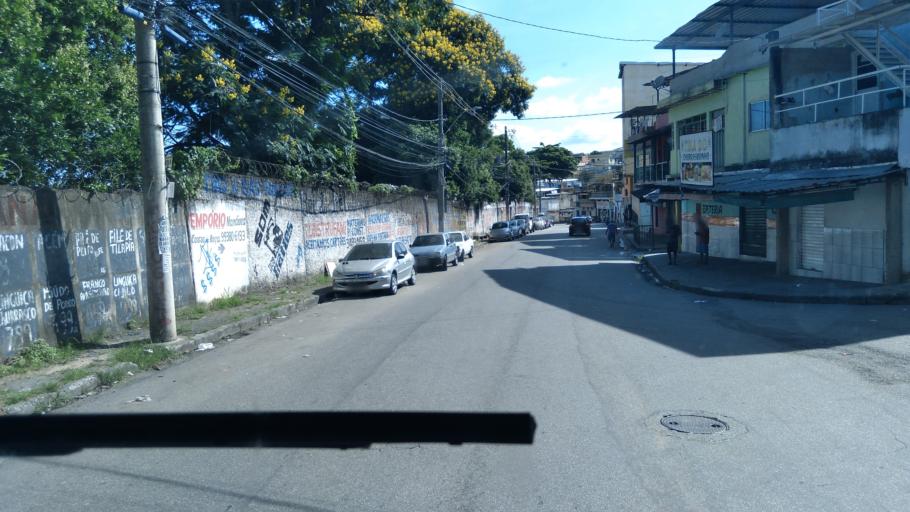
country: BR
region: Minas Gerais
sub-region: Belo Horizonte
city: Belo Horizonte
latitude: -19.8502
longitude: -43.8867
